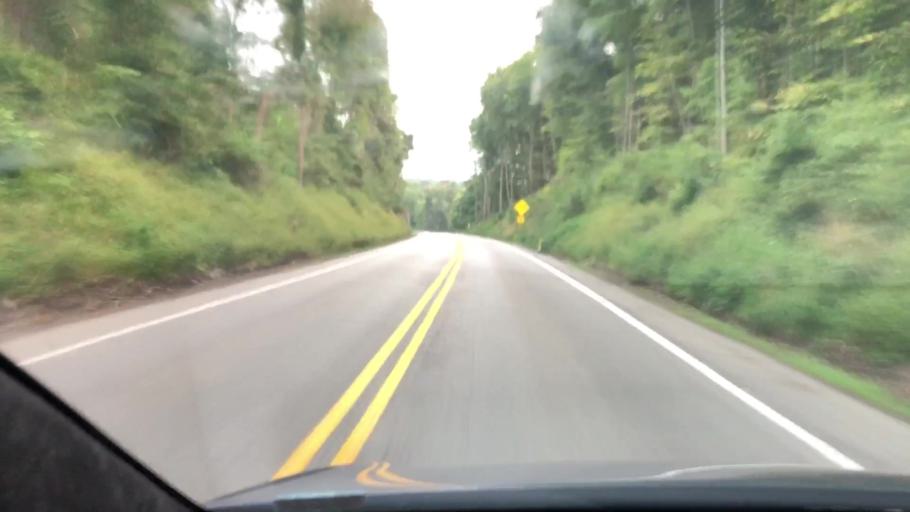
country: US
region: Pennsylvania
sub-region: Butler County
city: Slippery Rock
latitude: 41.0259
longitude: -80.0091
